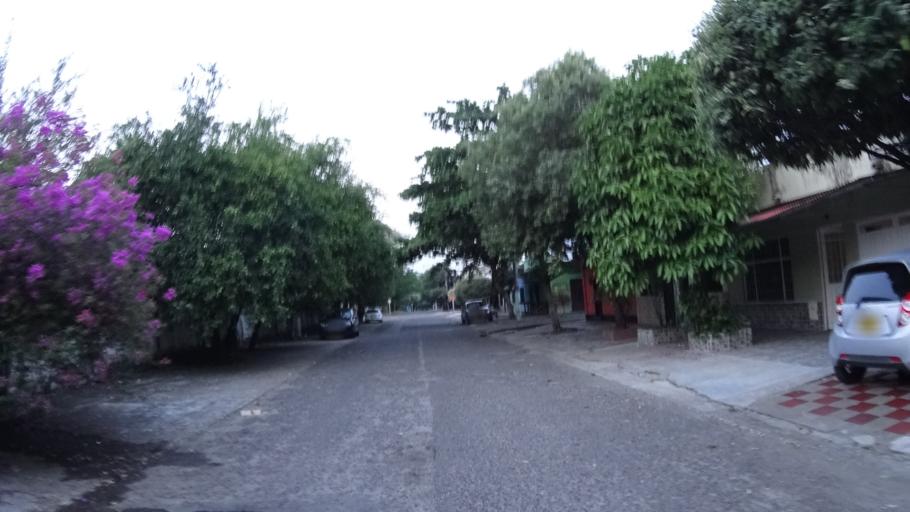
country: CO
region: Caldas
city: La Dorada
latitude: 5.4451
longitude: -74.6615
